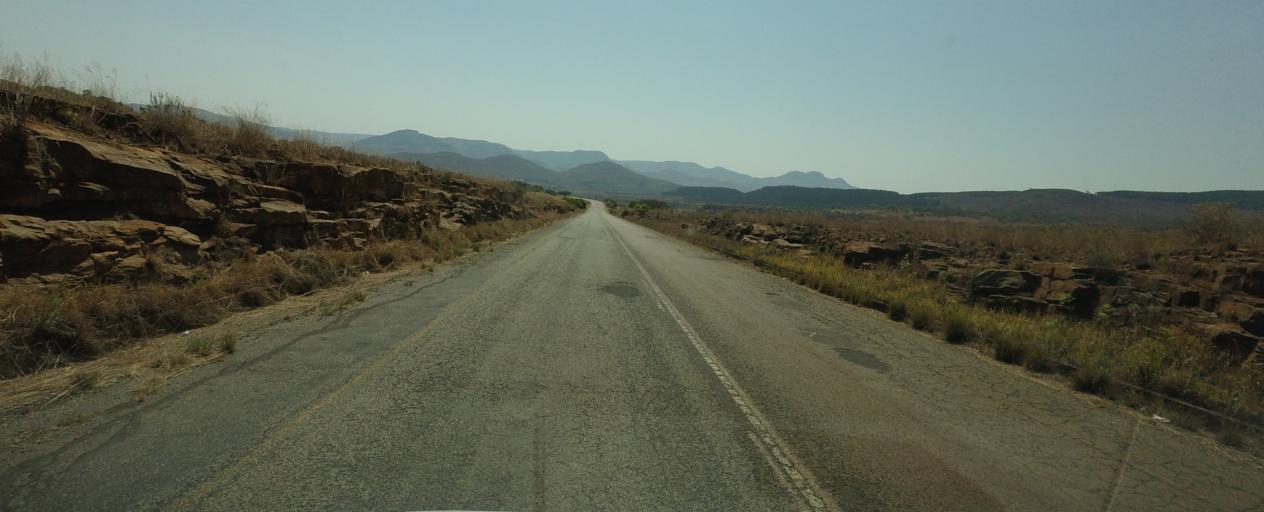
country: ZA
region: Mpumalanga
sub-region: Ehlanzeni District
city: Graksop
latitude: -24.7233
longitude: 30.8417
